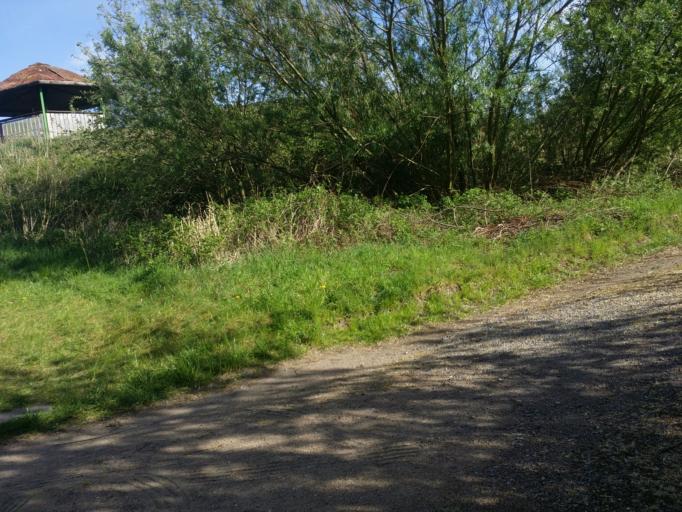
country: DE
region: Lower Saxony
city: Lemwerder
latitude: 53.1420
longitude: 8.6641
